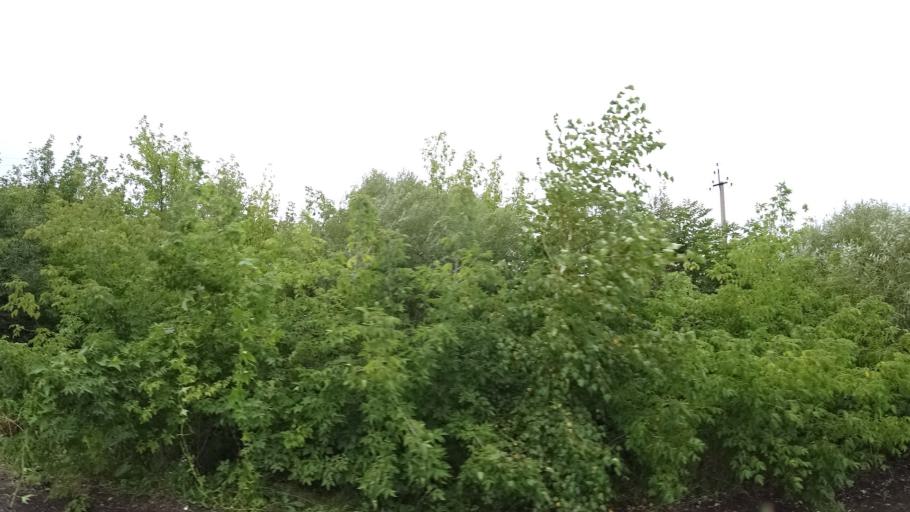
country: RU
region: Primorskiy
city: Chernigovka
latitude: 44.3358
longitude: 132.5616
